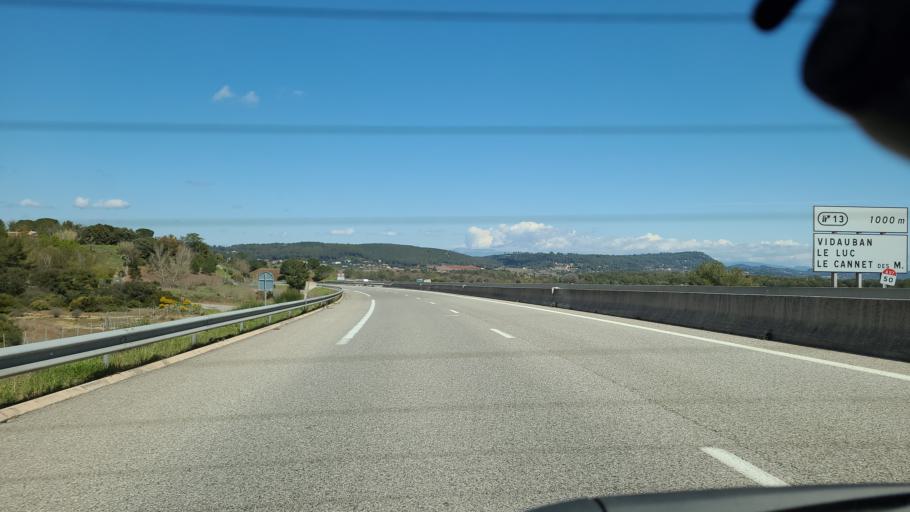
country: FR
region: Provence-Alpes-Cote d'Azur
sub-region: Departement du Var
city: Le Cannet-des-Maures
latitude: 43.3812
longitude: 6.3576
